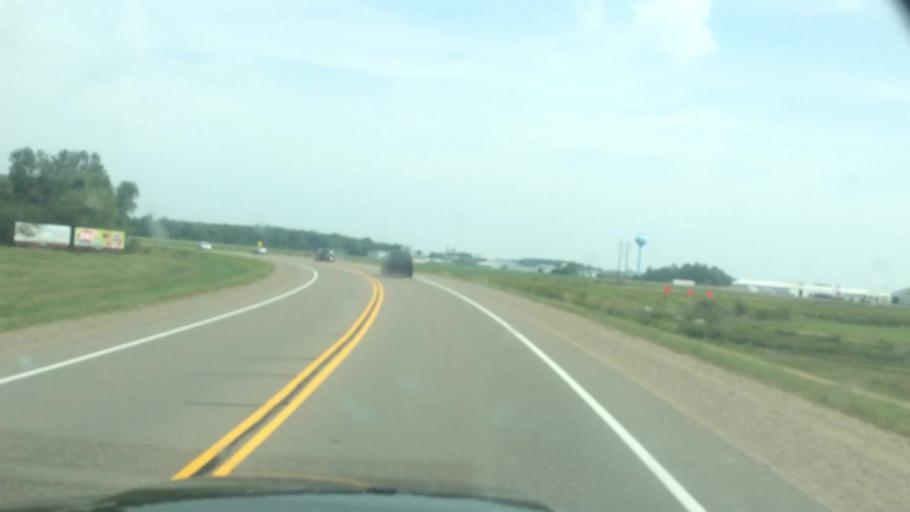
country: US
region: Wisconsin
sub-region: Langlade County
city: Antigo
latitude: 45.1568
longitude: -89.1624
